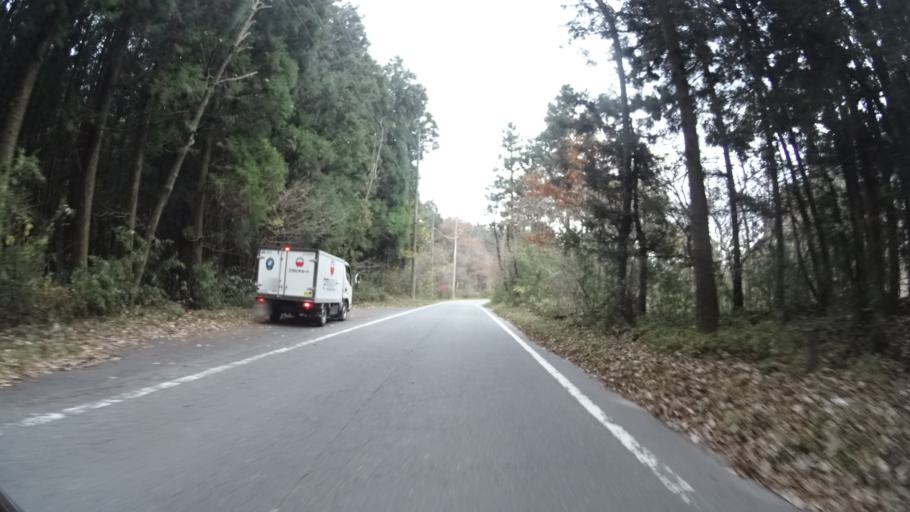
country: JP
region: Gunma
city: Omamacho-omama
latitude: 36.4872
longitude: 139.1863
